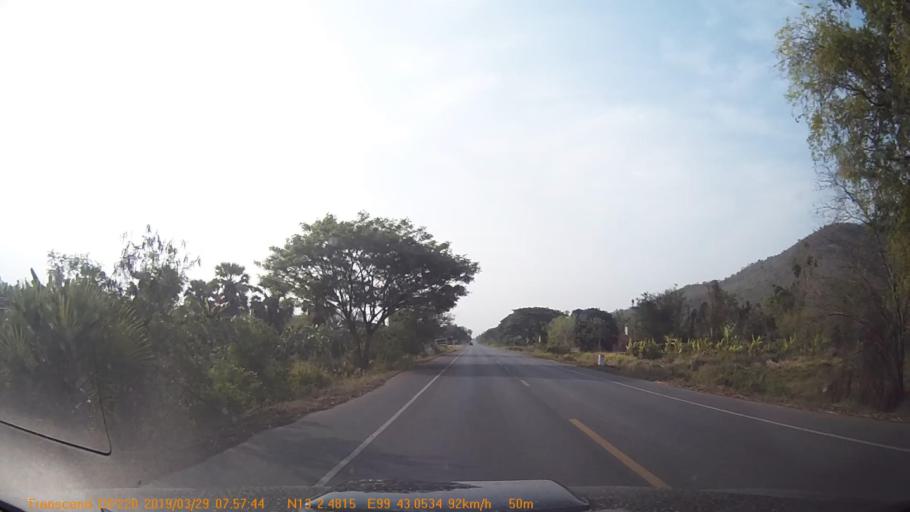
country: TH
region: Phetchaburi
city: Nong Ya Plong
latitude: 13.0410
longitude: 99.7178
